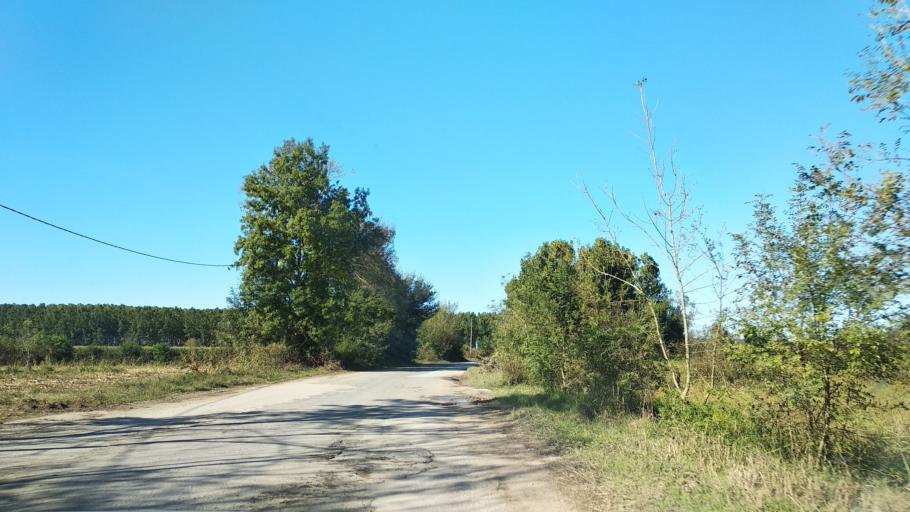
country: TR
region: Sakarya
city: Ortakoy
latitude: 41.0277
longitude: 30.6069
